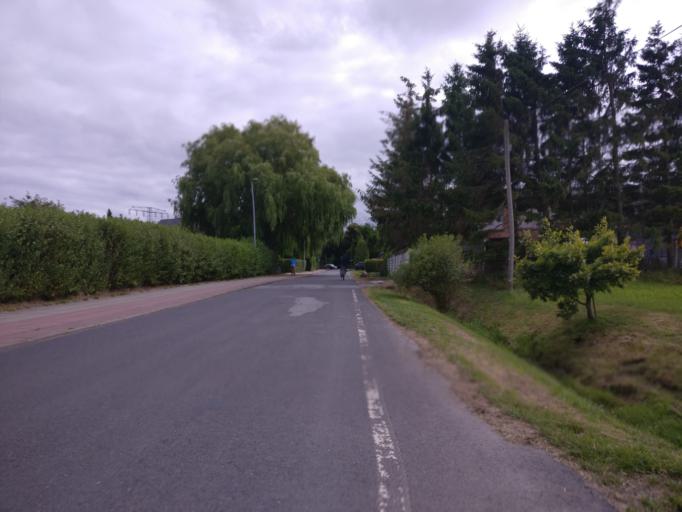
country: DE
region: Mecklenburg-Vorpommern
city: Warnemuende
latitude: 54.1599
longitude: 12.0573
